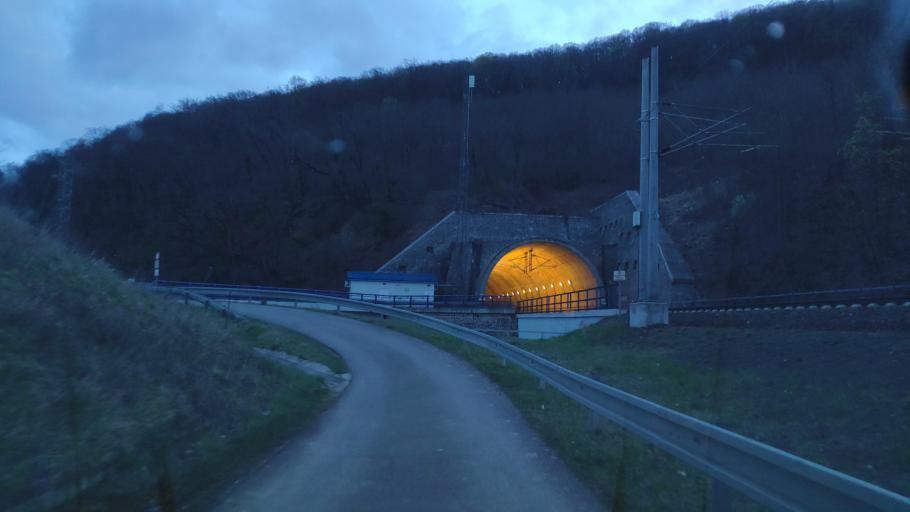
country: SK
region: Trenciansky
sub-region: Okres Nove Mesto nad Vahom
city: Nove Mesto nad Vahom
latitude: 48.7935
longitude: 17.8648
